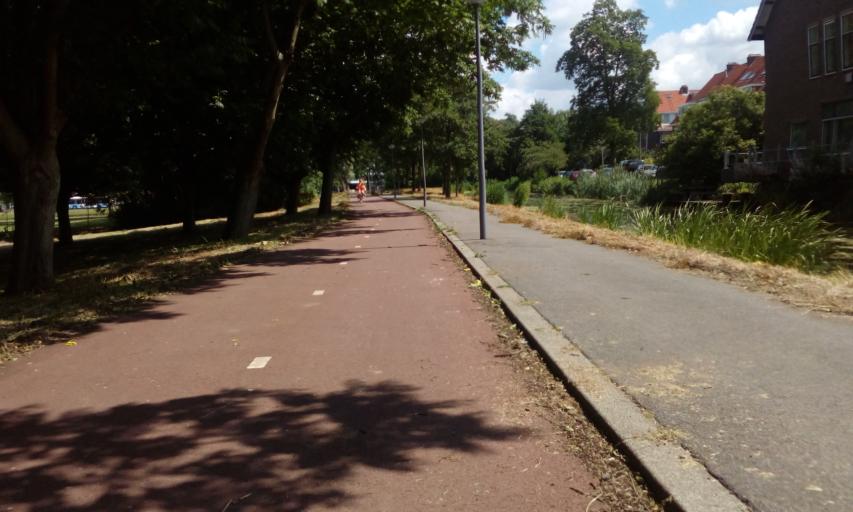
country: NL
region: South Holland
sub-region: Gemeente Lansingerland
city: Bergschenhoek
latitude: 51.9586
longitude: 4.4890
